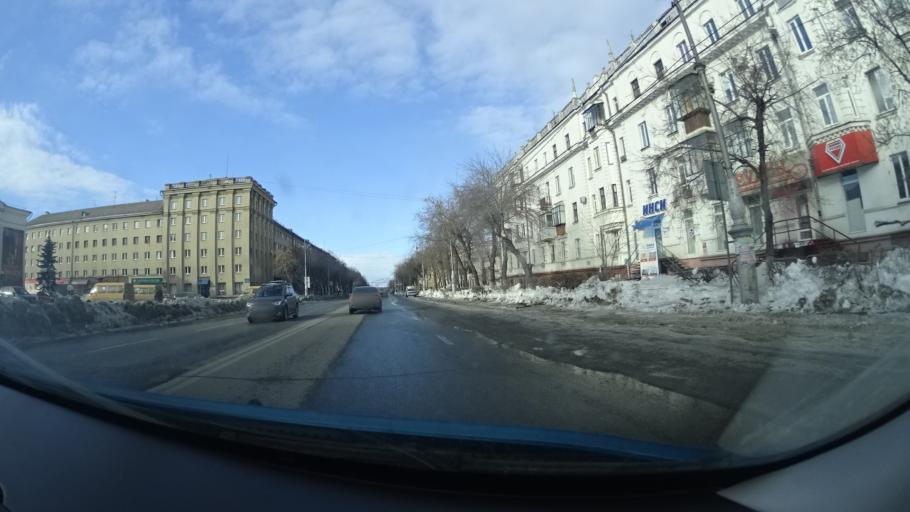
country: RU
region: Chelyabinsk
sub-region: Gorod Magnitogorsk
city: Magnitogorsk
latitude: 53.4298
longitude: 58.9837
